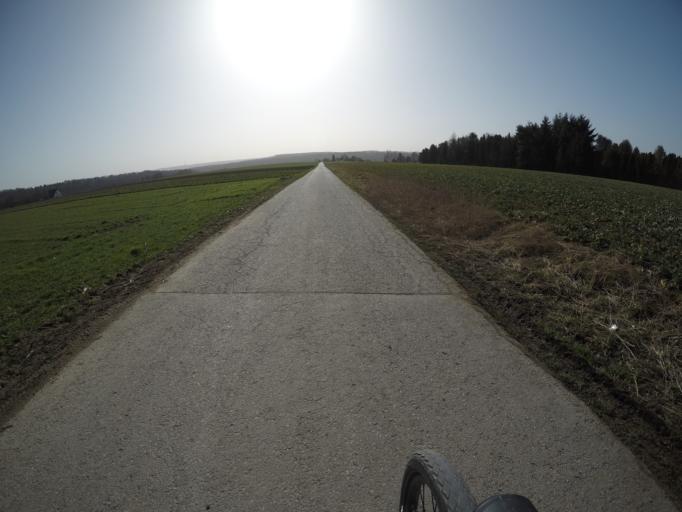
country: DE
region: Baden-Wuerttemberg
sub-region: Regierungsbezirk Stuttgart
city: Schonaich
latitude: 48.6620
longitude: 9.0752
